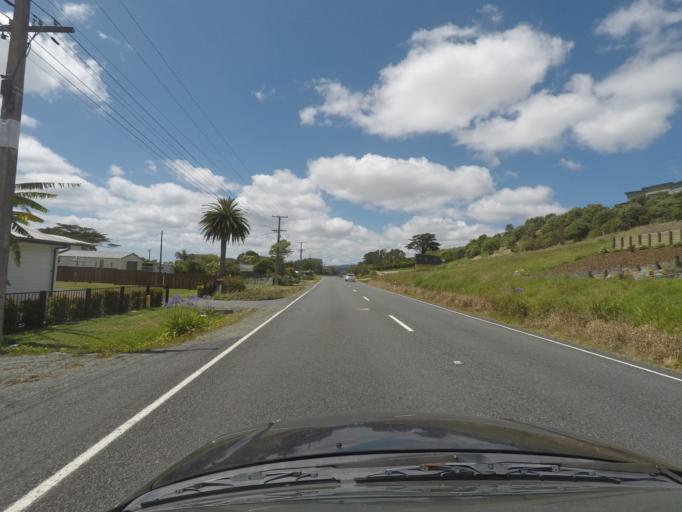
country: NZ
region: Northland
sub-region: Whangarei
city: Ruakaka
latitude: -35.9950
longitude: 174.4716
